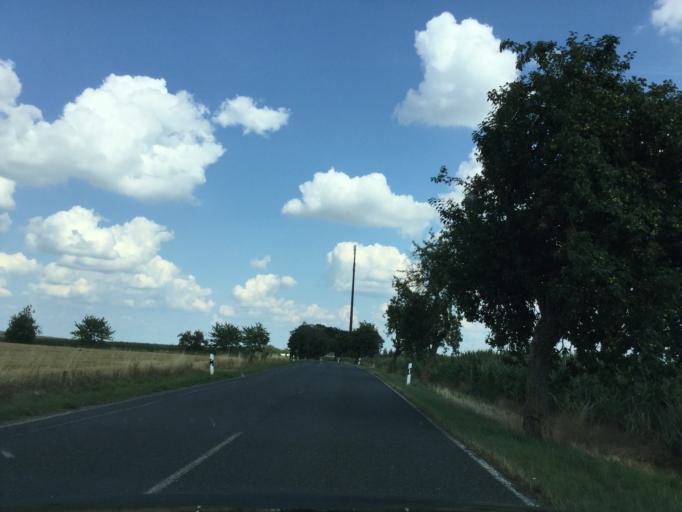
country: DE
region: Bavaria
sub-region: Regierungsbezirk Mittelfranken
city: Adelsdorf
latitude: 49.4802
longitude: 10.6966
